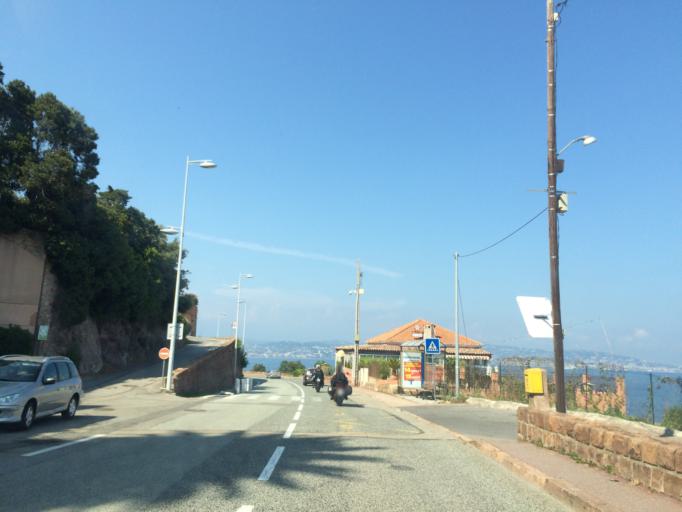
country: FR
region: Provence-Alpes-Cote d'Azur
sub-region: Departement des Alpes-Maritimes
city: Theoule-sur-Mer
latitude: 43.5009
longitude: 6.9529
